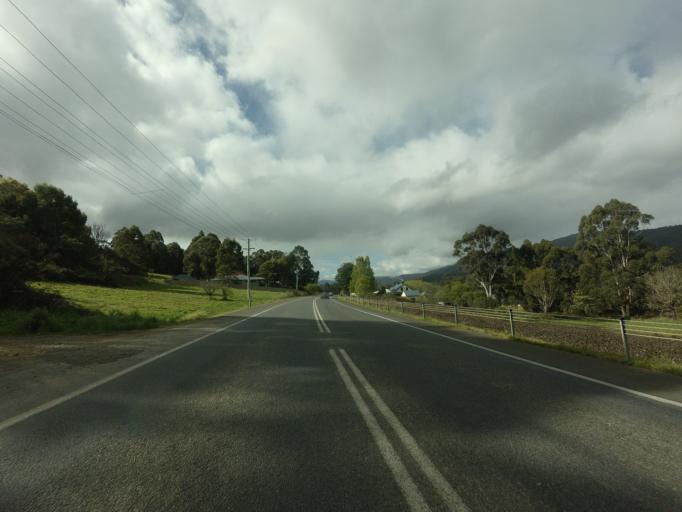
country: AU
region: Tasmania
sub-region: Huon Valley
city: Franklin
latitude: -43.0632
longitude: 147.0261
